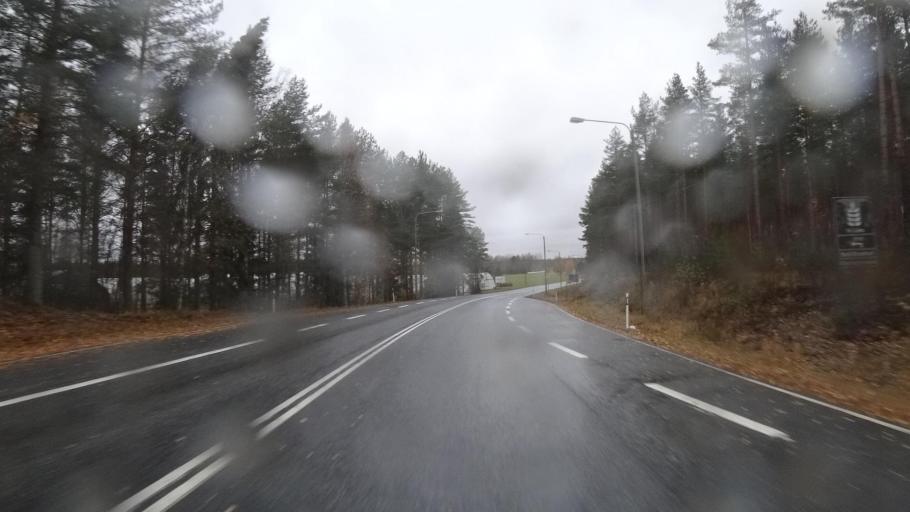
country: FI
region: Northern Savo
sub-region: Koillis-Savo
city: Tuusniemi
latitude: 62.8665
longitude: 28.3517
